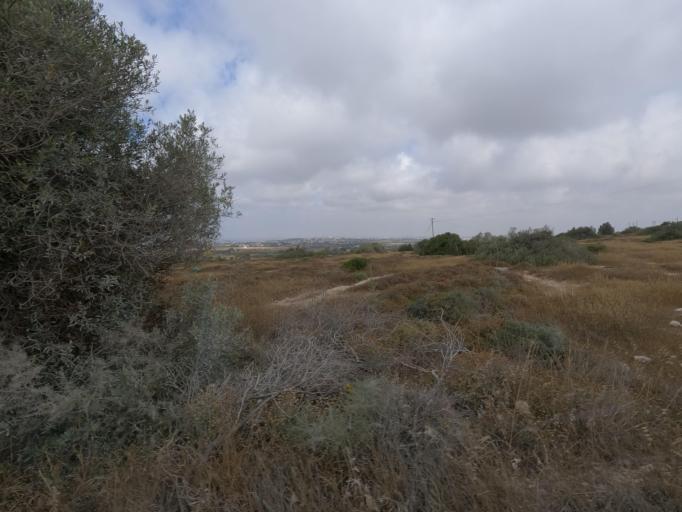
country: CY
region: Ammochostos
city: Protaras
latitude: 35.0031
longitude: 34.0304
